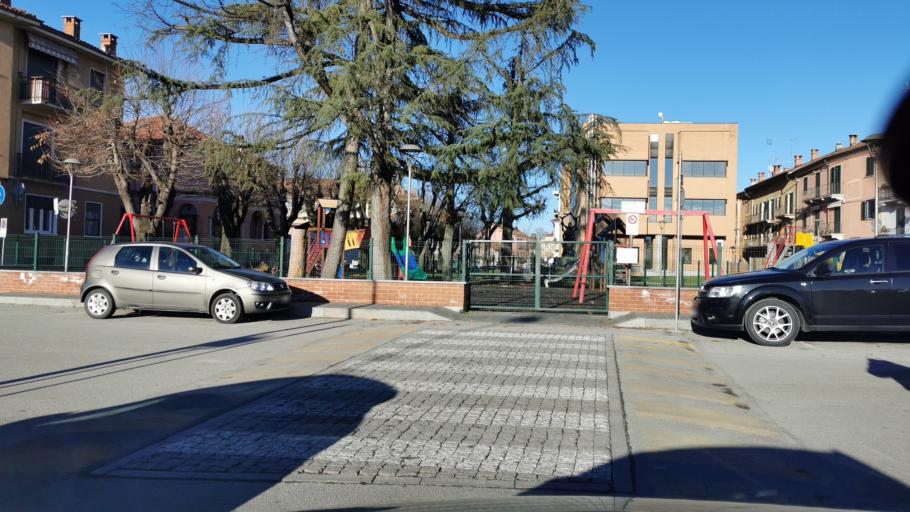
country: IT
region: Piedmont
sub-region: Provincia di Cuneo
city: Carru
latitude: 44.4782
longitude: 7.8769
